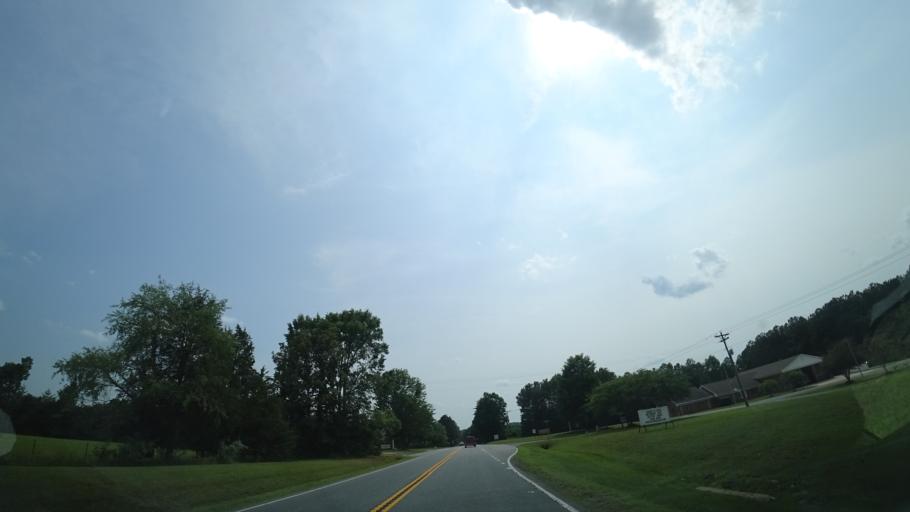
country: US
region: Virginia
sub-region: Spotsylvania County
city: Spotsylvania Courthouse
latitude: 38.1257
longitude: -77.7380
